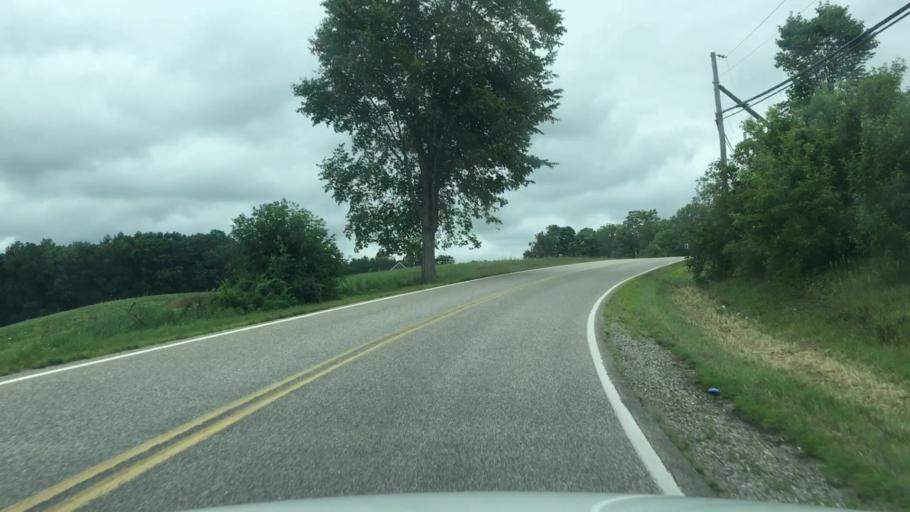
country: US
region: Maine
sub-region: York County
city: Biddeford
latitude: 43.5034
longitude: -70.5035
